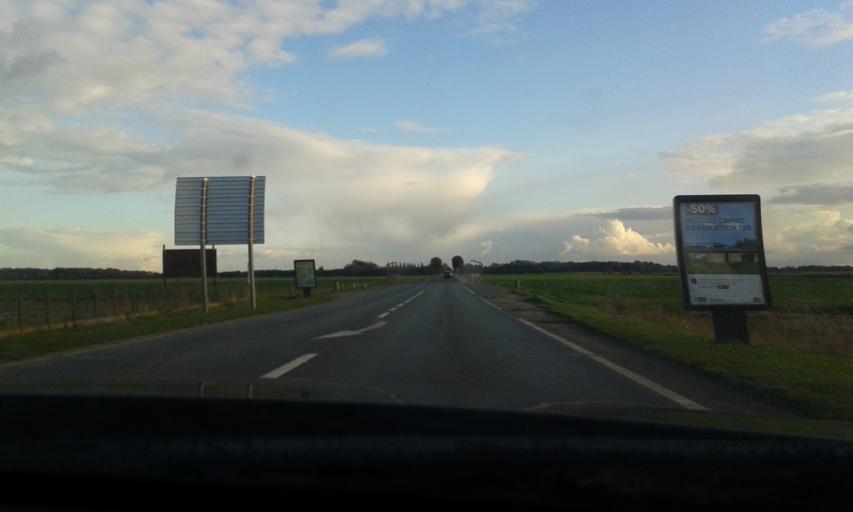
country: FR
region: Centre
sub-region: Departement d'Eure-et-Loir
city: Le Coudray
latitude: 48.4141
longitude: 1.5359
